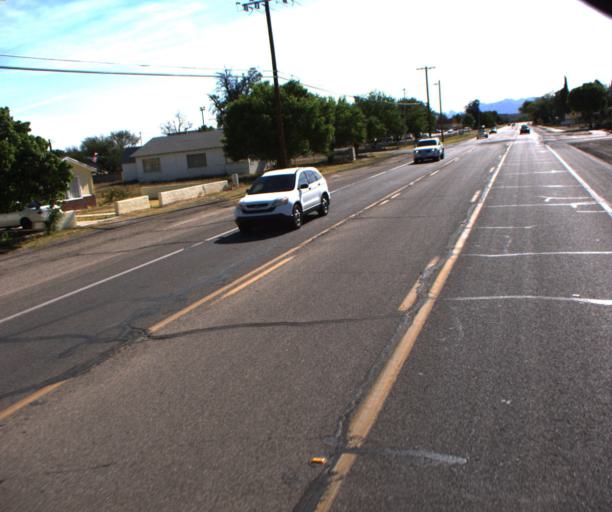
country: US
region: Arizona
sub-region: Cochise County
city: Saint David
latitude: 31.9052
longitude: -110.2230
